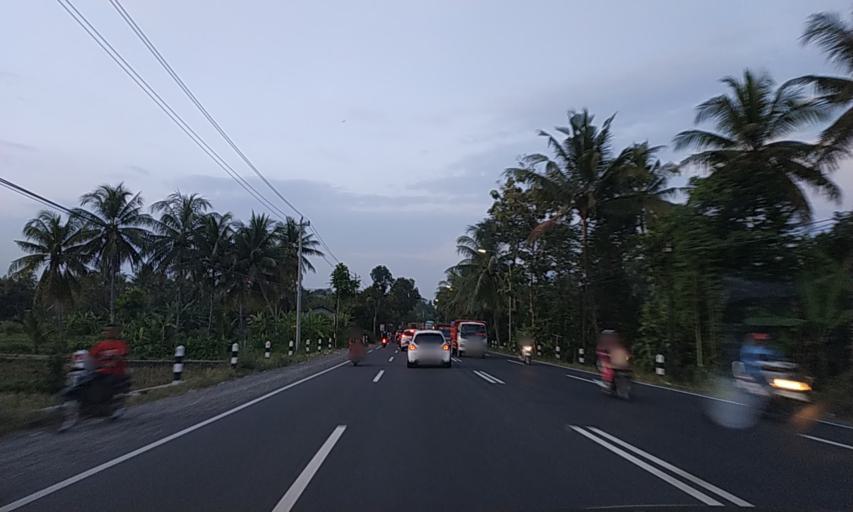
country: ID
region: Daerah Istimewa Yogyakarta
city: Srandakan
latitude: -7.8715
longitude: 110.2086
